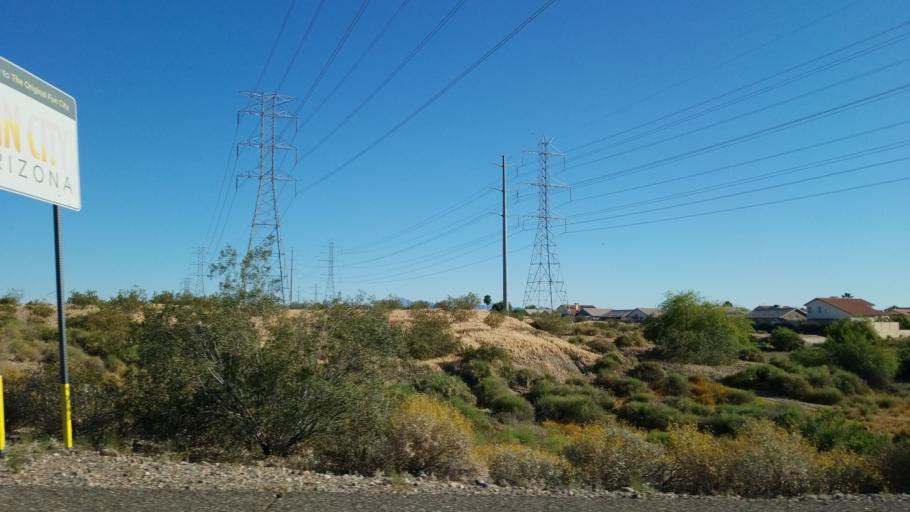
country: US
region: Arizona
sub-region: Maricopa County
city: Youngtown
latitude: 33.5654
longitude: -112.3003
